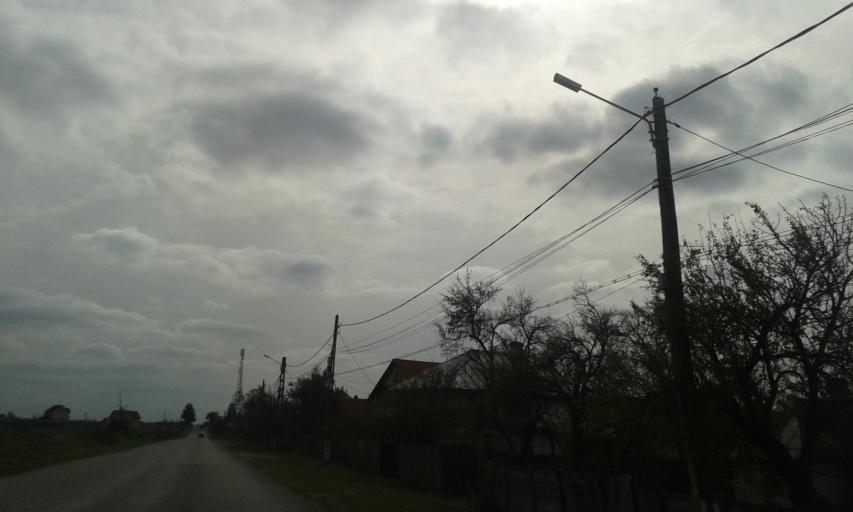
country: RO
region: Gorj
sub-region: Comuna Targu Carbunesti
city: Pojogeni
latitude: 44.9935
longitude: 23.4943
